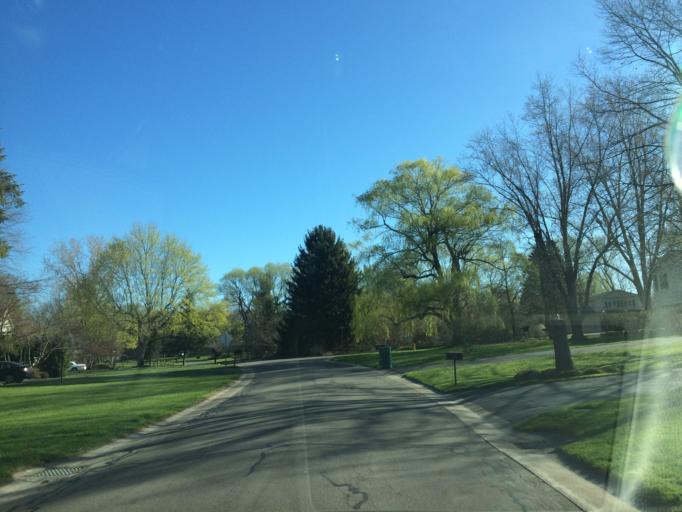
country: US
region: New York
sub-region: Monroe County
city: East Rochester
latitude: 43.0986
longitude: -77.4688
